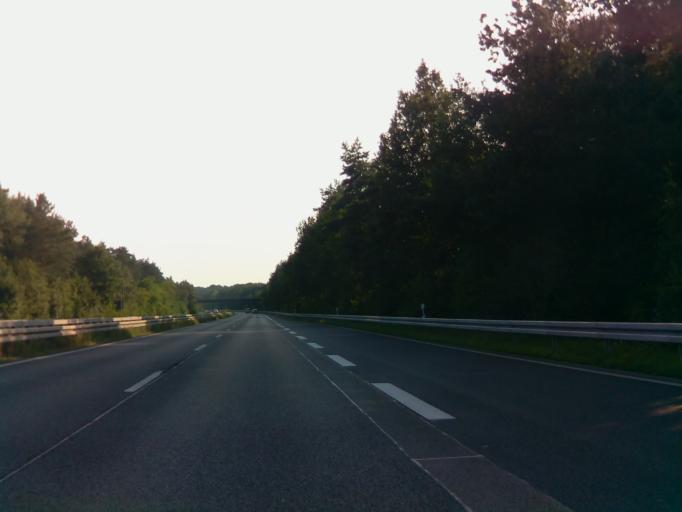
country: DE
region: Hesse
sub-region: Regierungsbezirk Darmstadt
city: Rodgau
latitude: 49.9955
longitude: 8.8866
